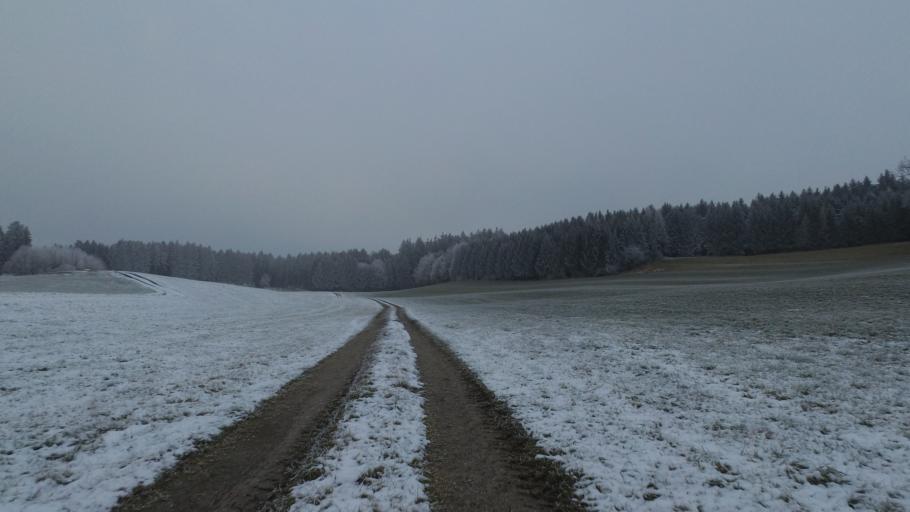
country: DE
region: Bavaria
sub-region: Upper Bavaria
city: Nussdorf
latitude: 47.8909
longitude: 12.5879
